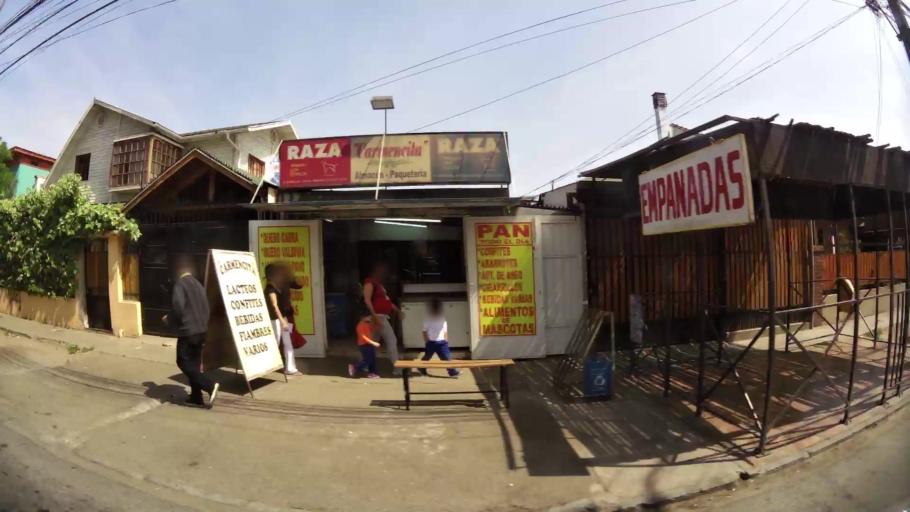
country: CL
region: Santiago Metropolitan
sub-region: Provincia de Santiago
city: Lo Prado
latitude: -33.4205
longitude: -70.6978
